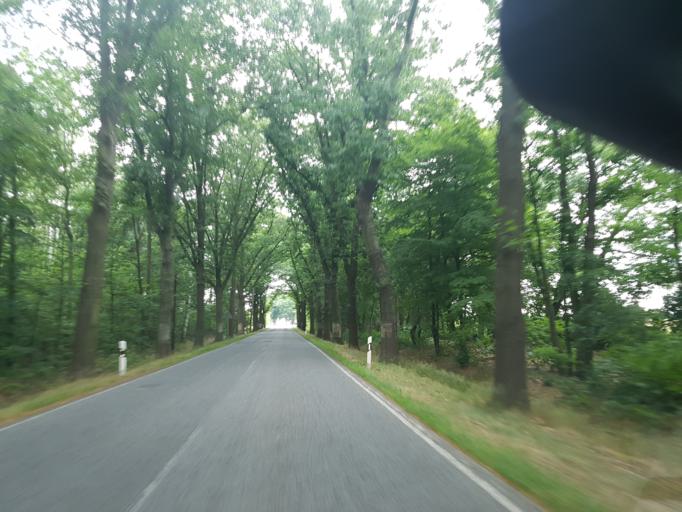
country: DE
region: Brandenburg
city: Dahme
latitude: 51.8452
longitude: 13.4116
